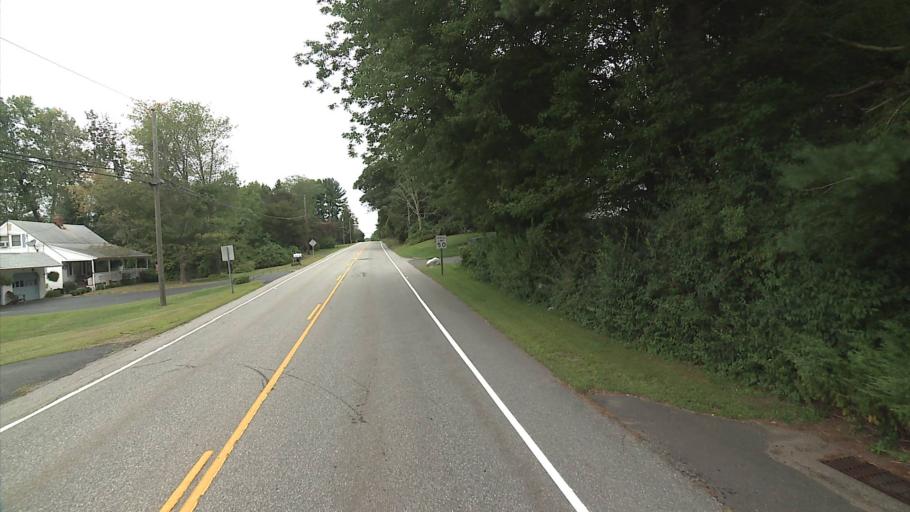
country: US
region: Connecticut
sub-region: Hartford County
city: Terramuggus
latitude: 41.7050
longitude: -72.4340
